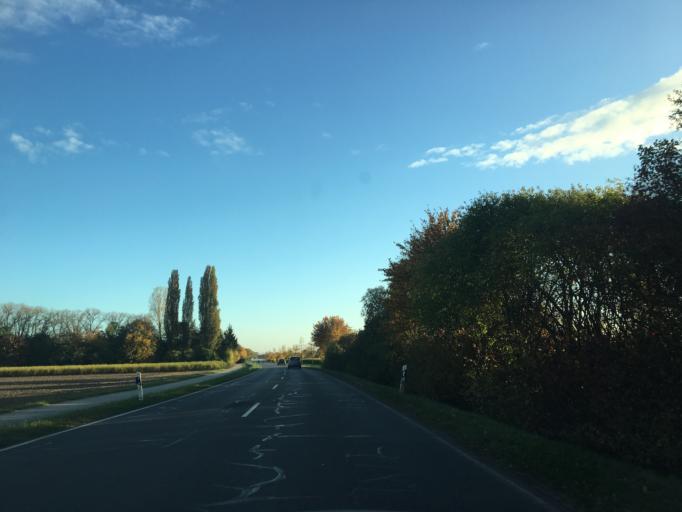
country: DE
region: Hesse
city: Zwingenberg
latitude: 49.7160
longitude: 8.6046
